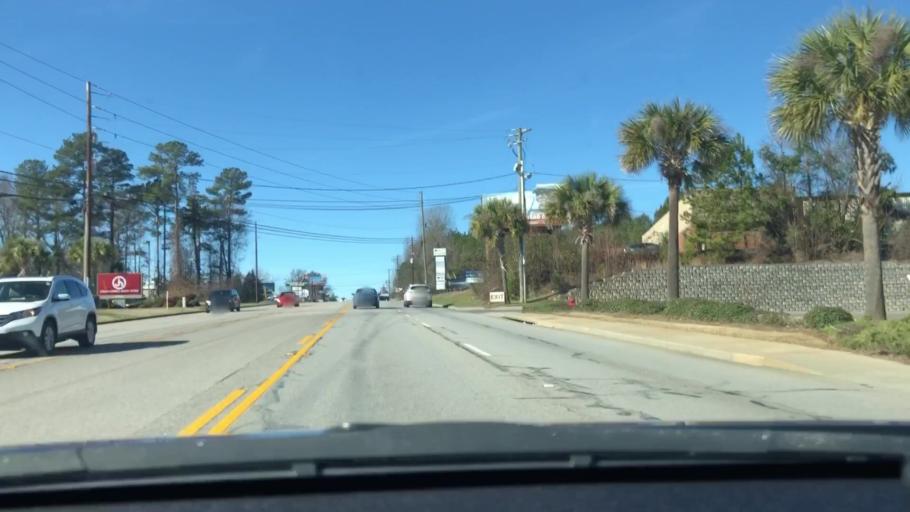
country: US
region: South Carolina
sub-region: Lexington County
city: Oak Grove
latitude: 34.0130
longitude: -81.1741
